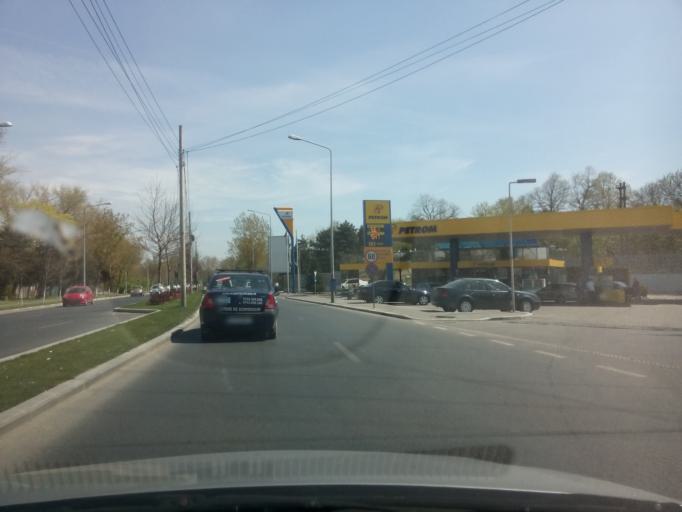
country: RO
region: Ilfov
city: Dobroesti
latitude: 44.4413
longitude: 26.1915
